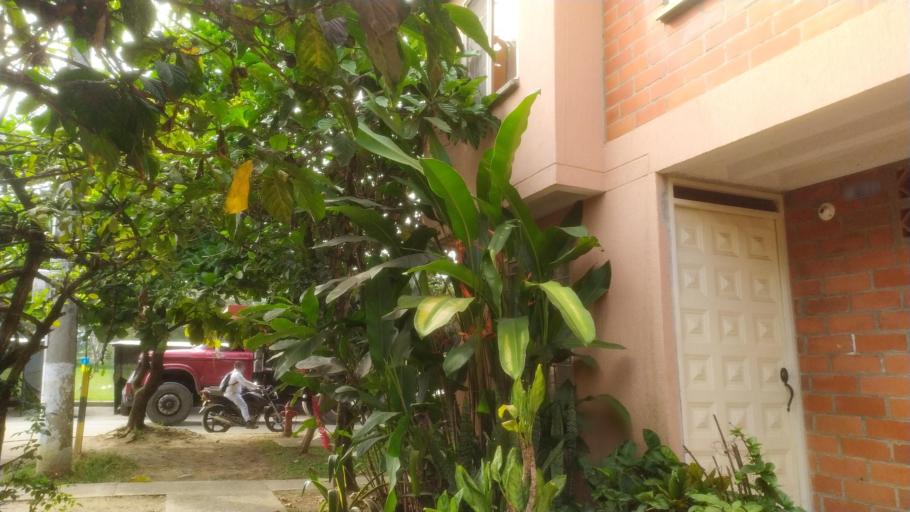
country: CO
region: Valle del Cauca
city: Jamundi
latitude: 3.2388
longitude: -76.5071
